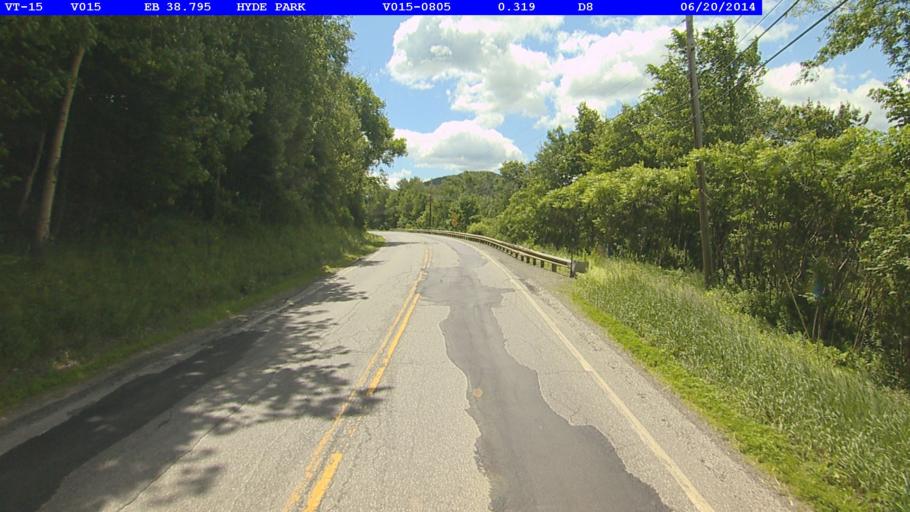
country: US
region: Vermont
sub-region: Lamoille County
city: Hyde Park
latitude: 44.6054
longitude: -72.6427
